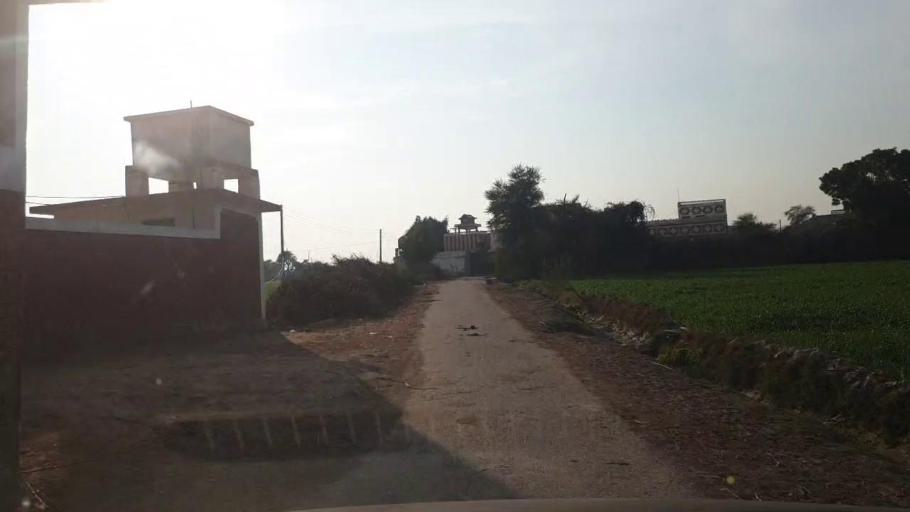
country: PK
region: Sindh
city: Shahpur Chakar
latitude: 26.1652
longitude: 68.6375
